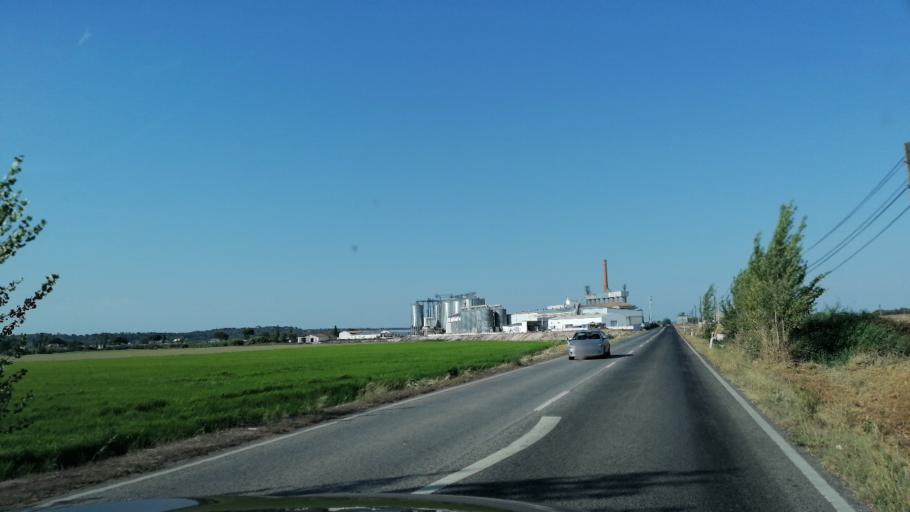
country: PT
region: Santarem
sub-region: Coruche
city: Coruche
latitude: 38.9422
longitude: -8.5040
